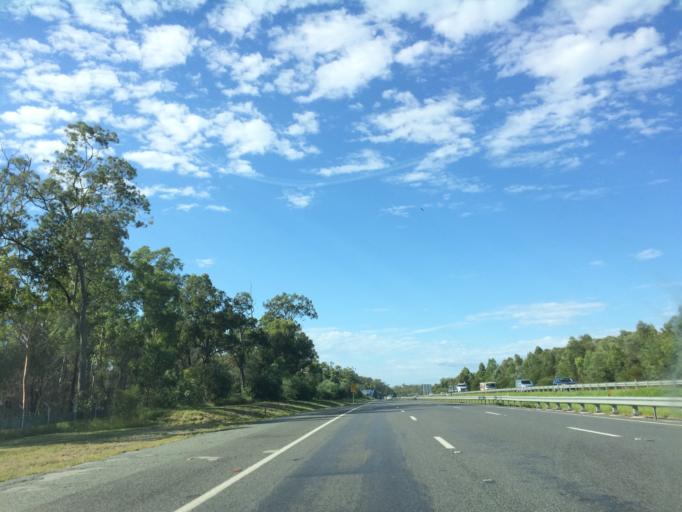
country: AU
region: Queensland
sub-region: Brisbane
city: Forest Lake
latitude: -27.6323
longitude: 152.9402
